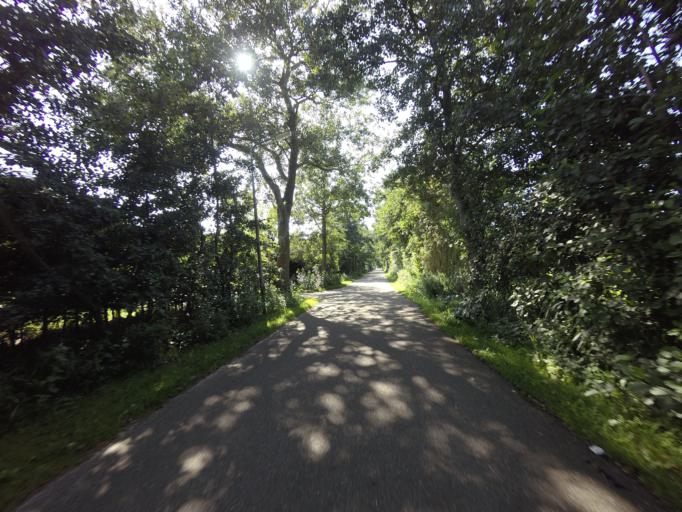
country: NL
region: Friesland
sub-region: Gemeente Terschelling
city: West-Terschelling
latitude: 53.3936
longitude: 5.3109
